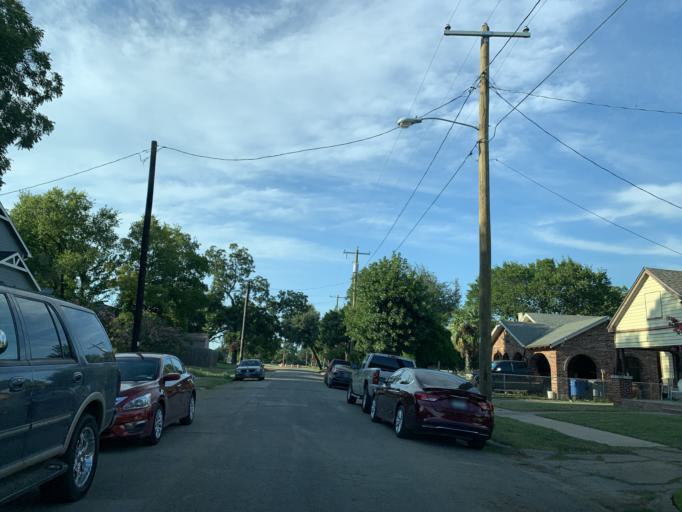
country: US
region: Texas
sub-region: Dallas County
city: Dallas
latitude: 32.7386
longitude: -96.8216
